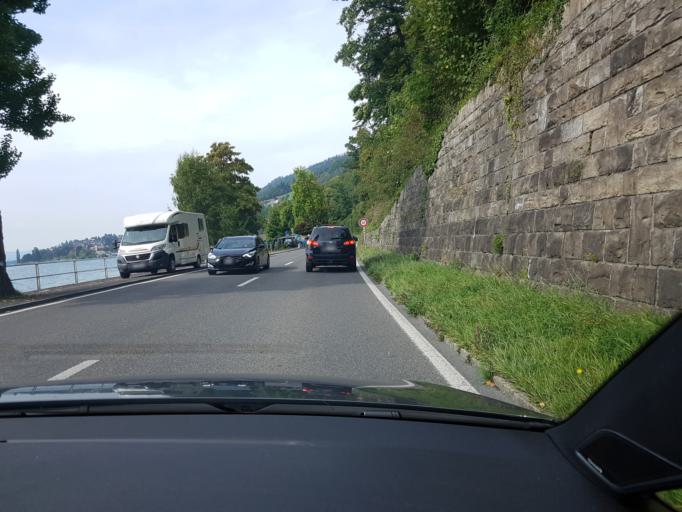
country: CH
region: Bern
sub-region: Thun District
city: Sigriswil
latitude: 46.7197
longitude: 7.6858
